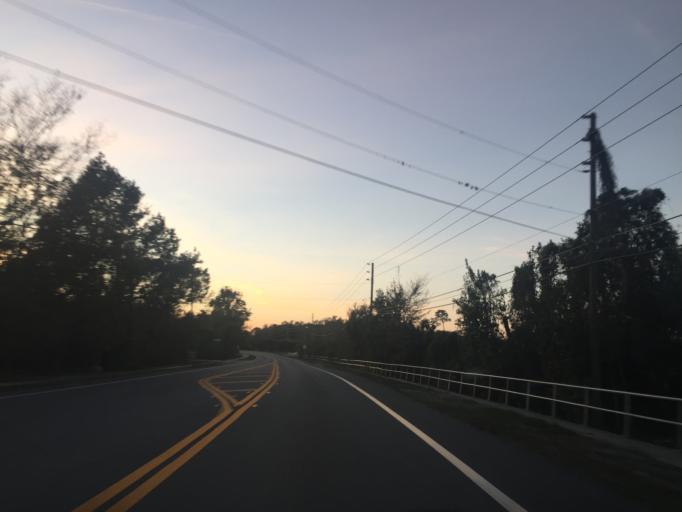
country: US
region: Florida
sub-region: Seminole County
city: Oviedo
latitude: 28.6700
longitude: -81.1909
